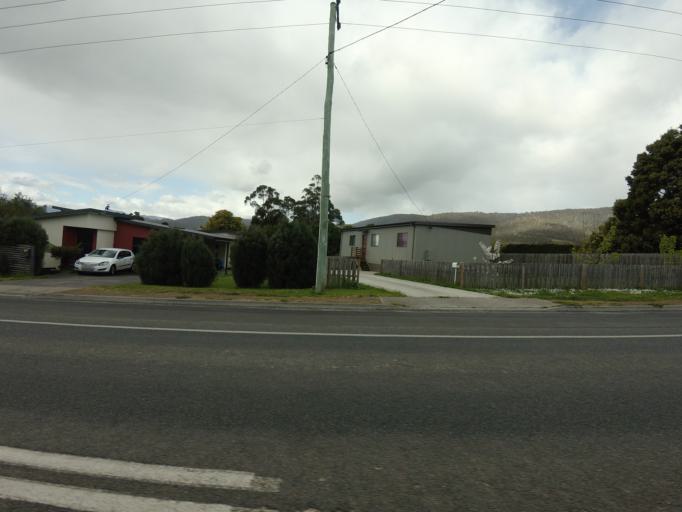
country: AU
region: Tasmania
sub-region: Huon Valley
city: Huonville
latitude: -43.0366
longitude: 147.0460
